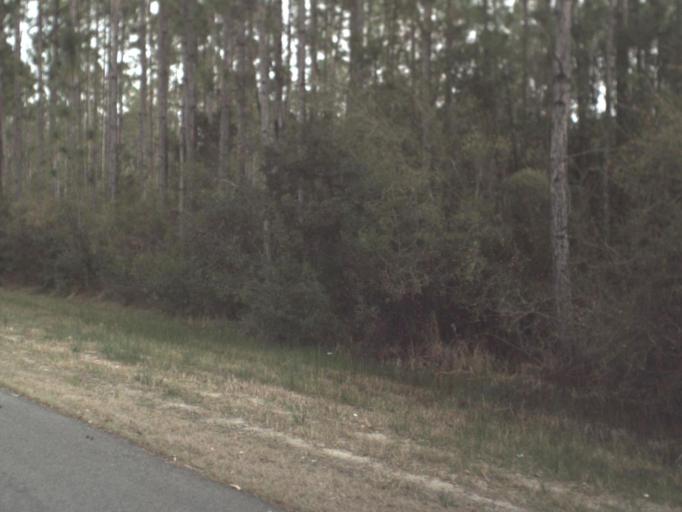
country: US
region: Florida
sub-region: Bay County
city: Callaway
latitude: 30.1527
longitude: -85.5154
